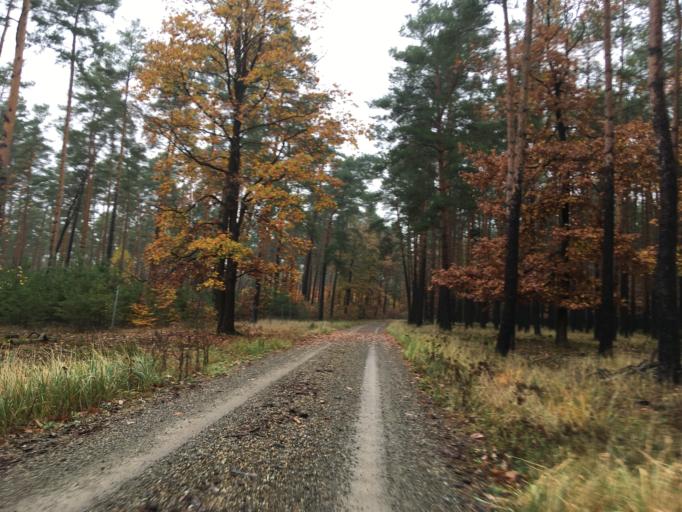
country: DE
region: Brandenburg
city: Beeskow
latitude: 52.2498
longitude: 14.2912
